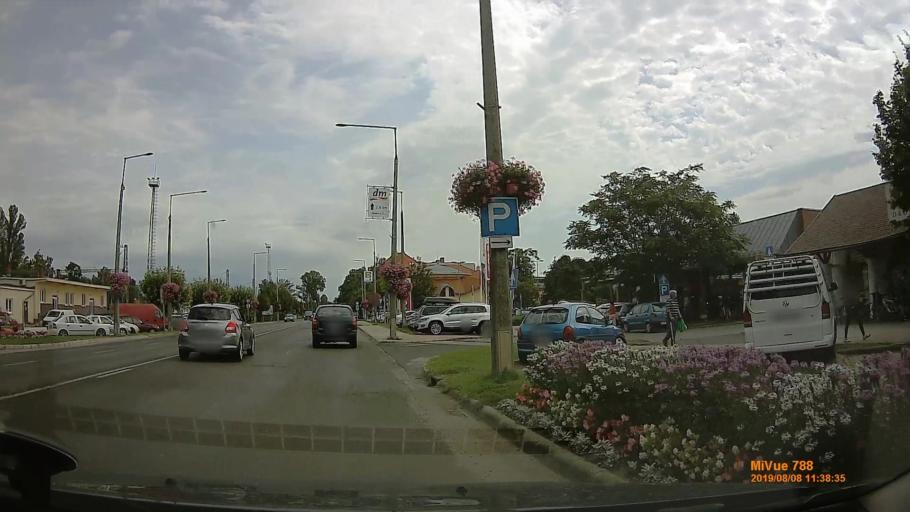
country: HU
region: Somogy
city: Fonyod
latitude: 46.7496
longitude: 17.5582
